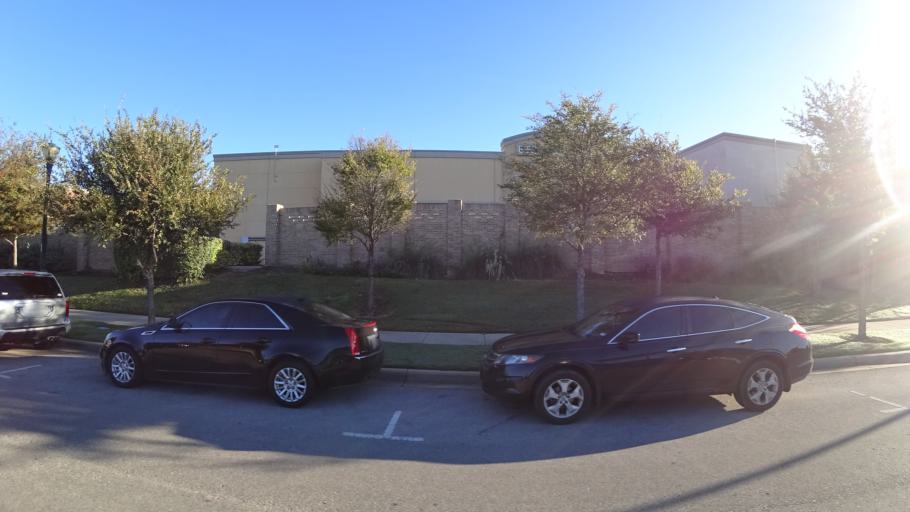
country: US
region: Texas
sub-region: Travis County
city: Austin
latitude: 30.3037
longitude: -97.7094
